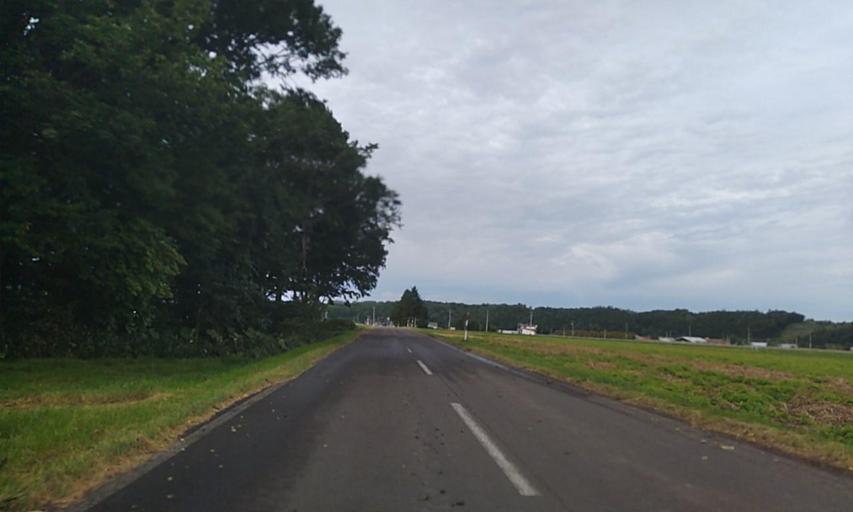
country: JP
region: Hokkaido
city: Abashiri
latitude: 43.7949
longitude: 144.5469
